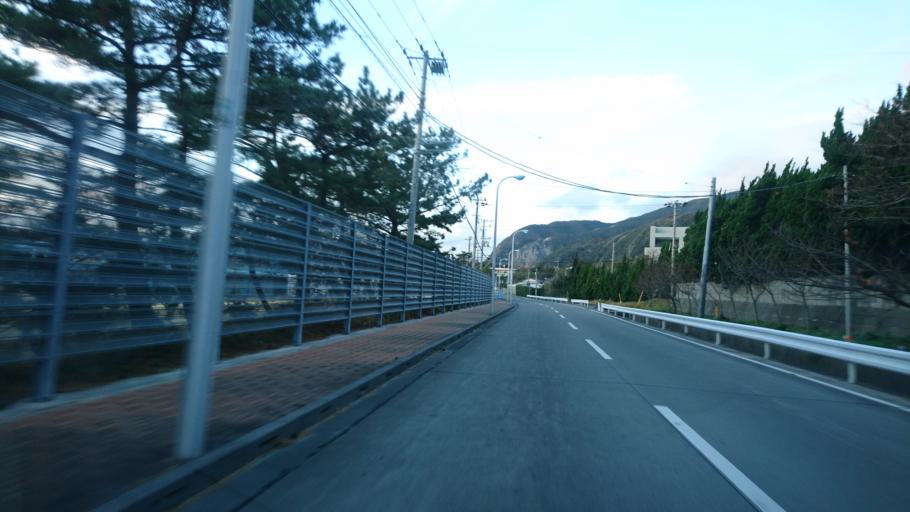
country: JP
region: Shizuoka
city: Shimoda
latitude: 34.3709
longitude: 139.2591
